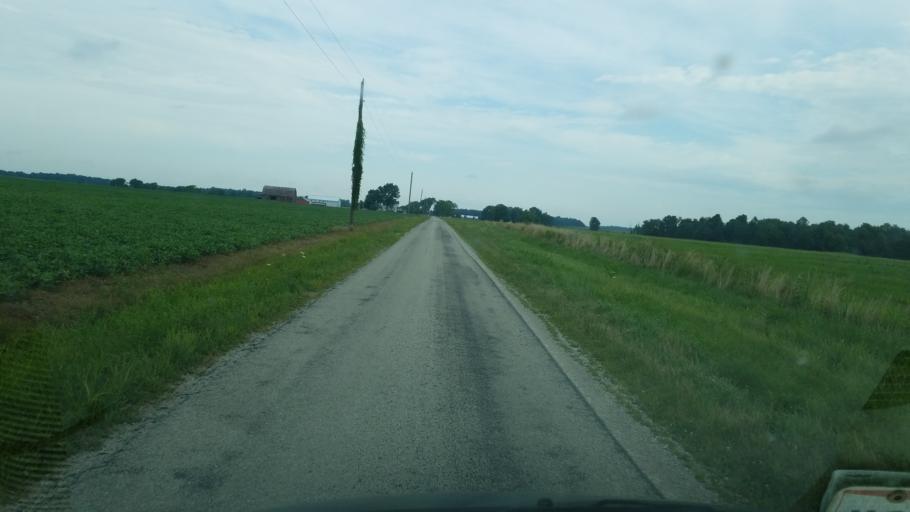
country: US
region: Ohio
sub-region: Seneca County
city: Tiffin
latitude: 40.9808
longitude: -83.0551
